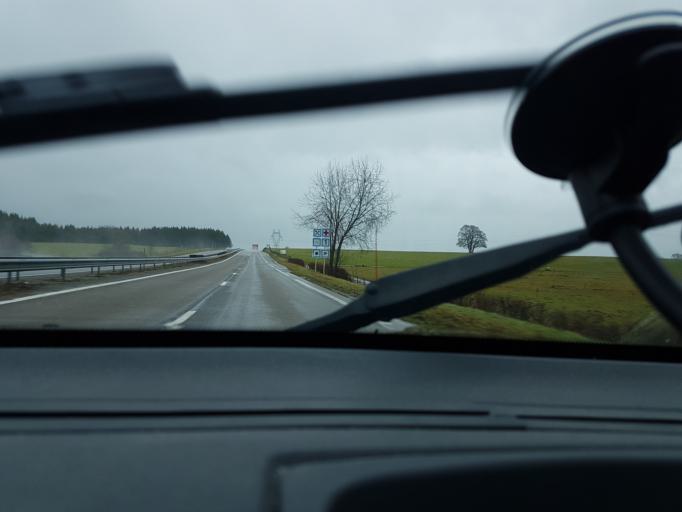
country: FR
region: Franche-Comte
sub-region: Departement du Doubs
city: Vercel-Villedieu-le-Camp
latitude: 47.1395
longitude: 6.4073
